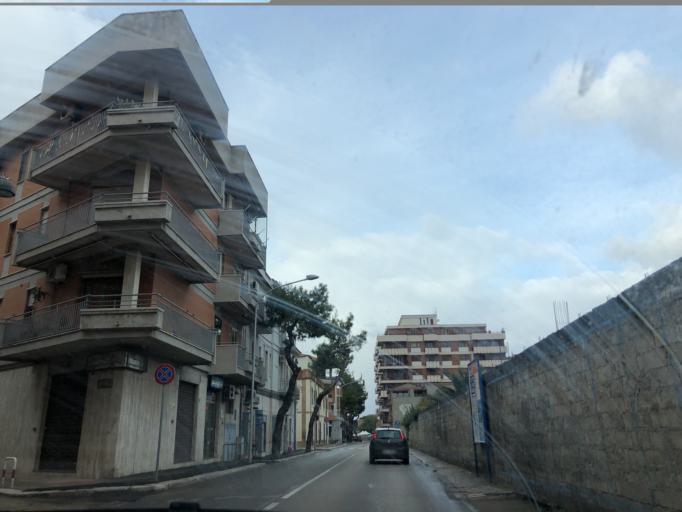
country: IT
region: Apulia
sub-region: Provincia di Foggia
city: Lucera
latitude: 41.5080
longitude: 15.3313
